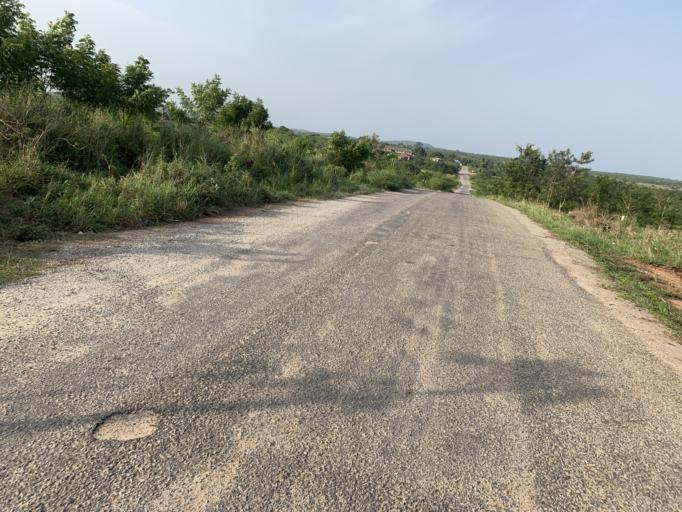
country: GH
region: Central
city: Winneba
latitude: 5.3865
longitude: -0.6048
